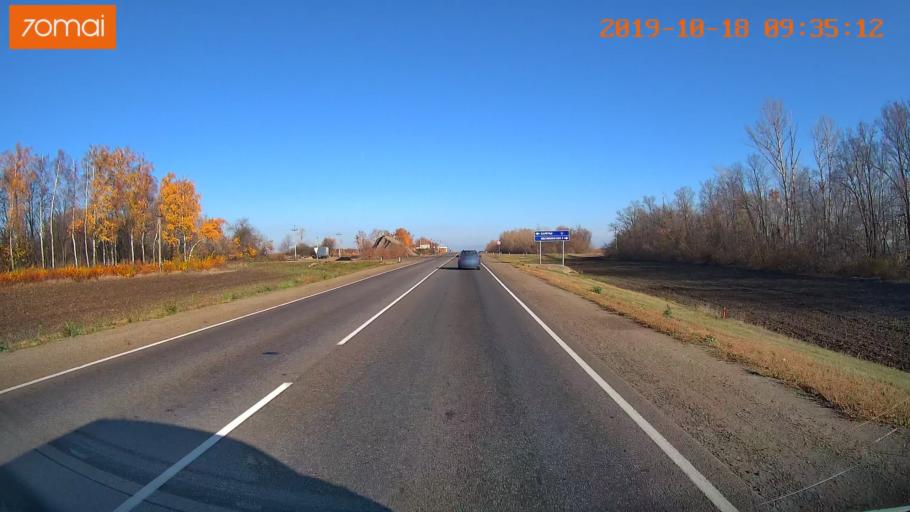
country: RU
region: Tula
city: Yefremov
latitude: 53.1895
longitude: 38.1493
